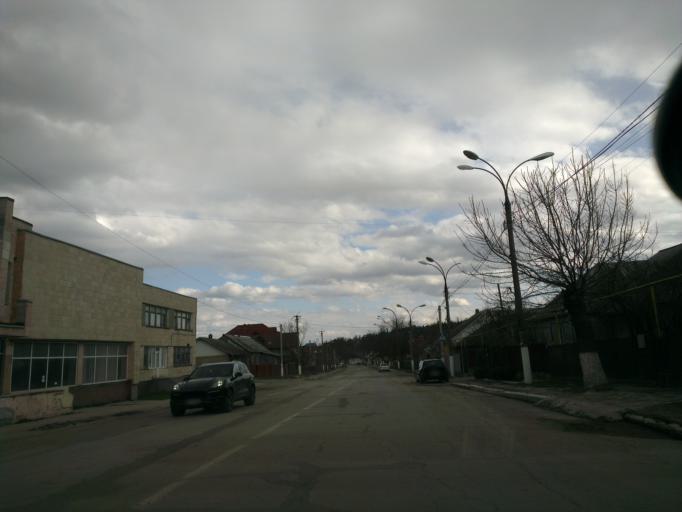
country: MD
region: Hincesti
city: Hincesti
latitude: 46.8220
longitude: 28.5974
